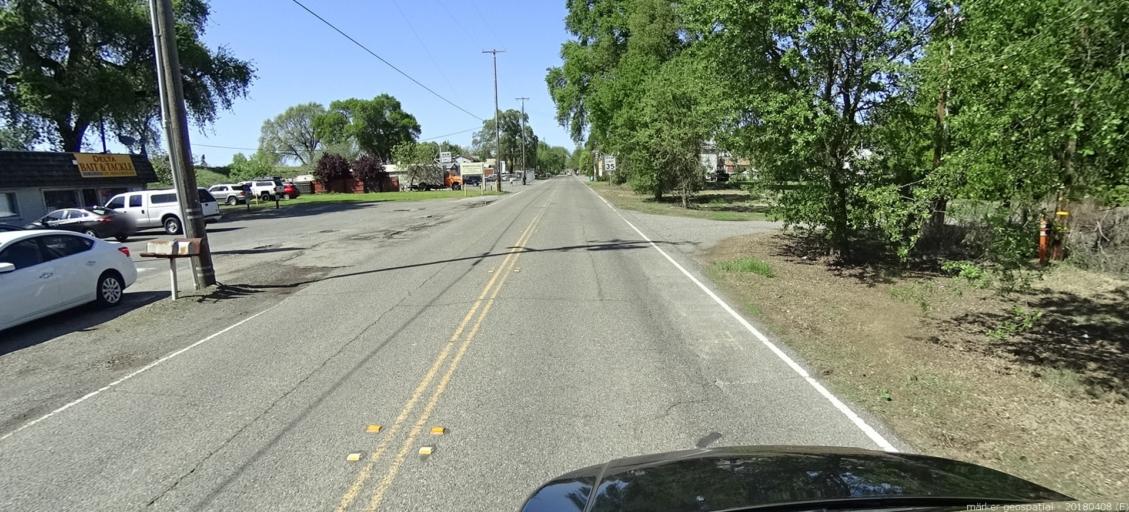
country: US
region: California
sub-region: Sacramento County
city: Parkway
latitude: 38.4606
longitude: -121.5016
